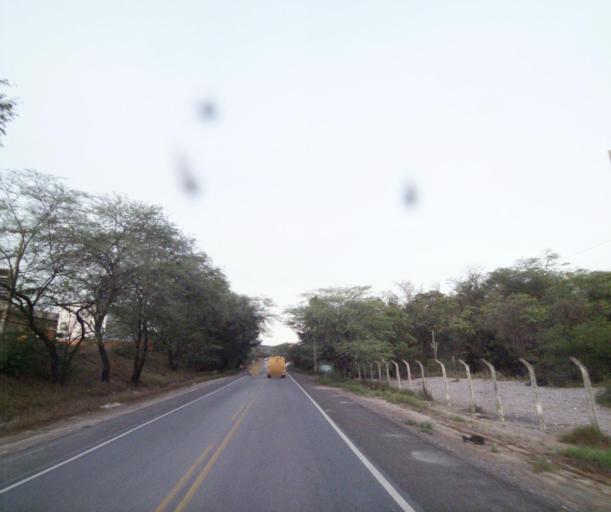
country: BR
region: Bahia
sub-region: Brumado
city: Brumado
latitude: -14.2425
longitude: -41.7257
